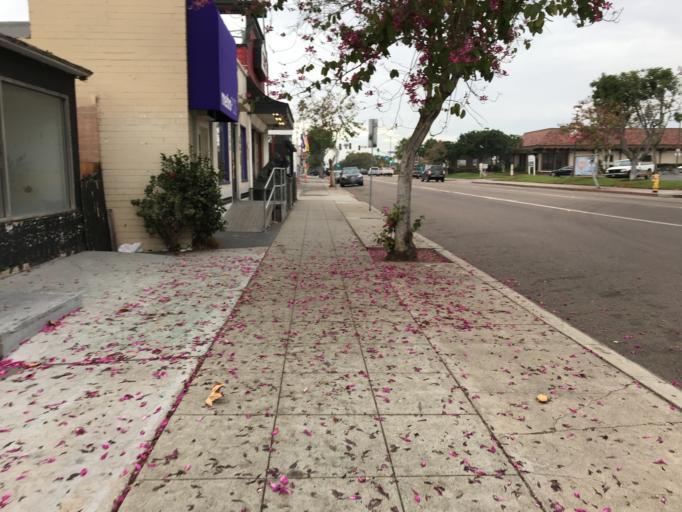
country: US
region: California
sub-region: San Diego County
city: La Jolla
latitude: 32.8005
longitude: -117.2375
